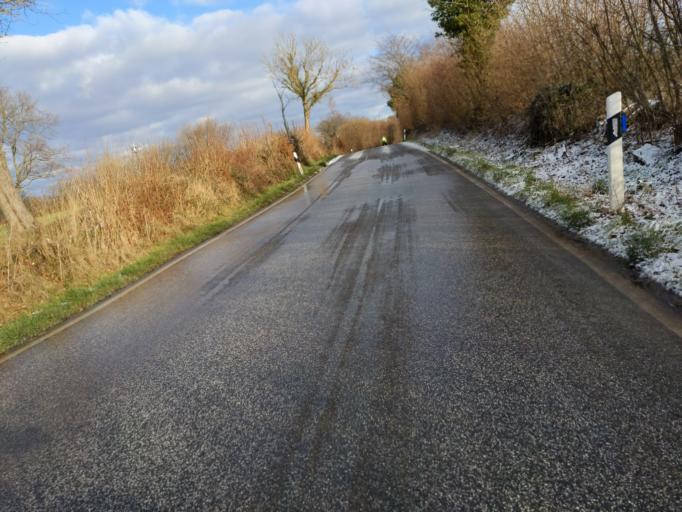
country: DE
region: Schleswig-Holstein
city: Travemuende
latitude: 53.9737
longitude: 10.8636
